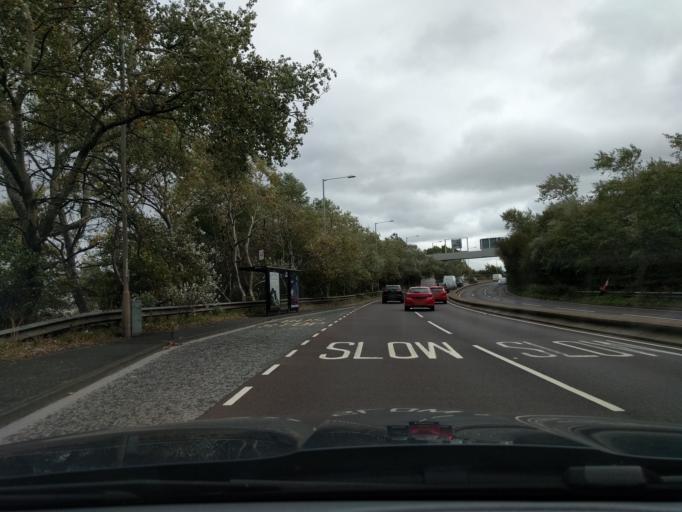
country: GB
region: England
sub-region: Newcastle upon Tyne
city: Benwell
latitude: 54.9652
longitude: -1.6877
